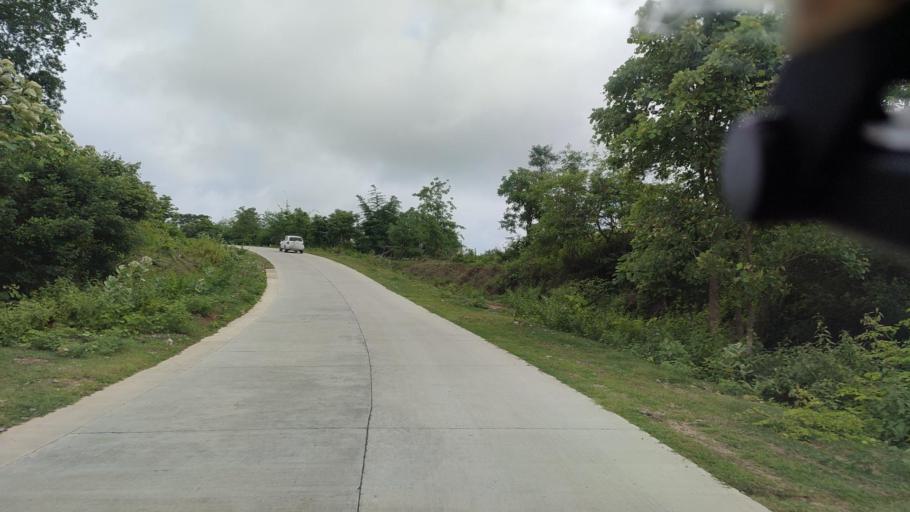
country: MM
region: Magway
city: Taungdwingyi
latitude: 20.0437
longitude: 95.7798
